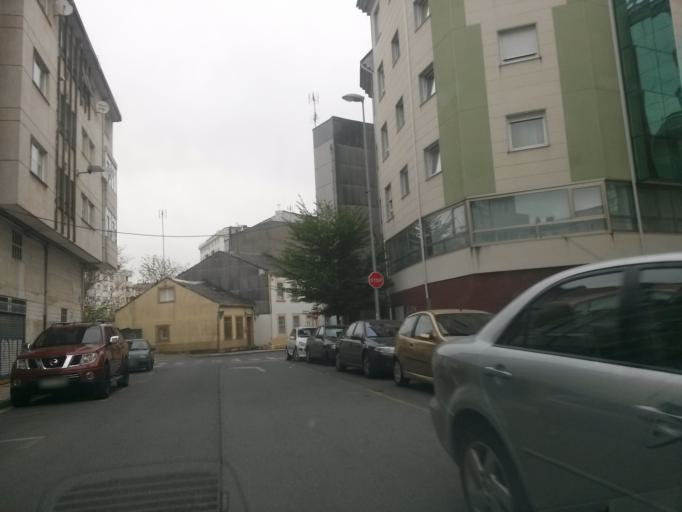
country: ES
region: Galicia
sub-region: Provincia de Lugo
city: Lugo
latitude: 43.0255
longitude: -7.5690
